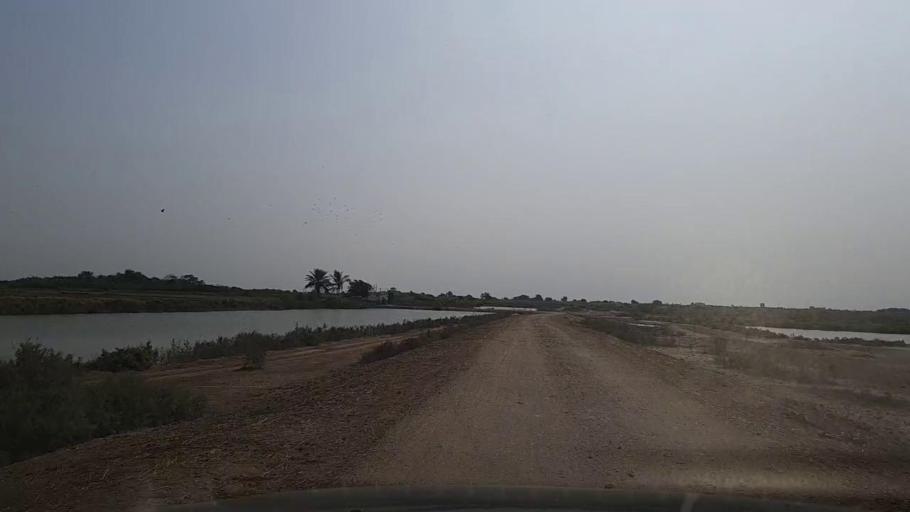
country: PK
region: Sindh
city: Thatta
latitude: 24.5708
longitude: 67.9170
